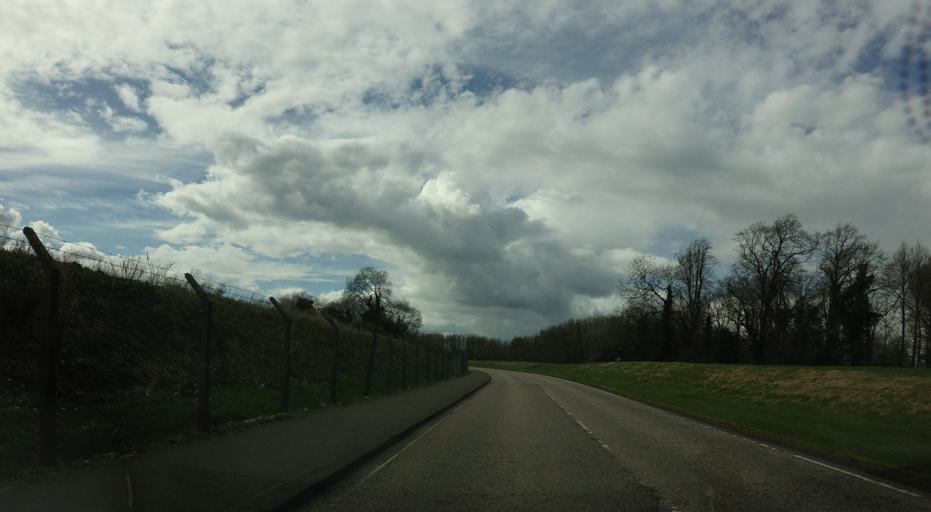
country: GB
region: Scotland
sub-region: Edinburgh
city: Edinburgh
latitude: 55.9782
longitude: -3.2570
